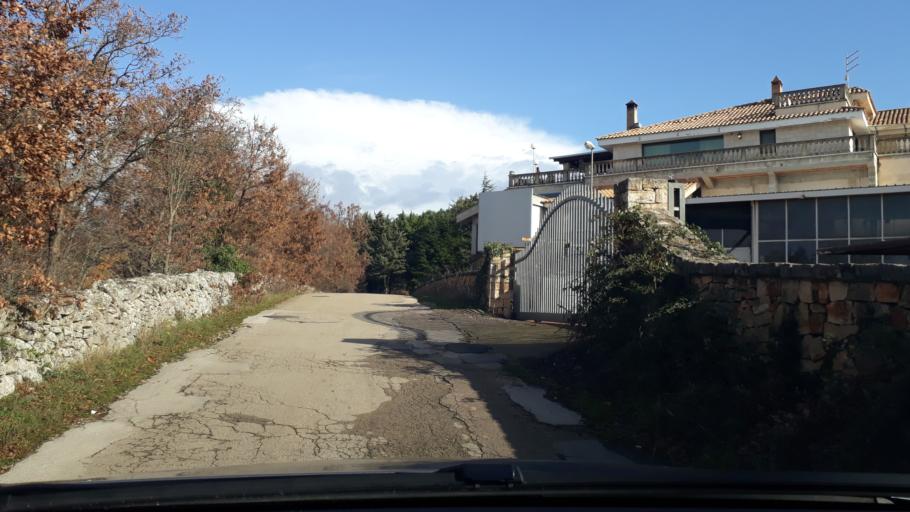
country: IT
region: Apulia
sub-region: Provincia di Brindisi
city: Cisternino
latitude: 40.6926
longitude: 17.4143
